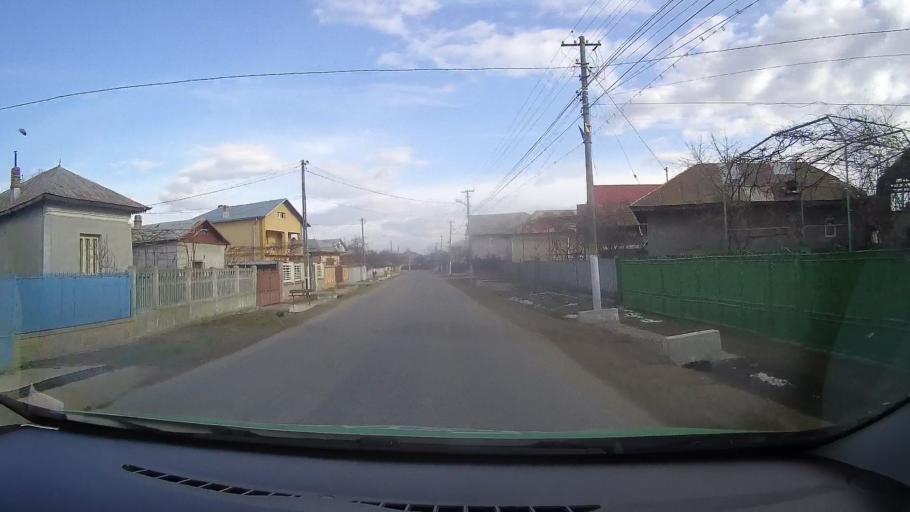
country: RO
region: Dambovita
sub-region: Comuna Comisani
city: Lazuri
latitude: 44.8685
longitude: 25.5252
